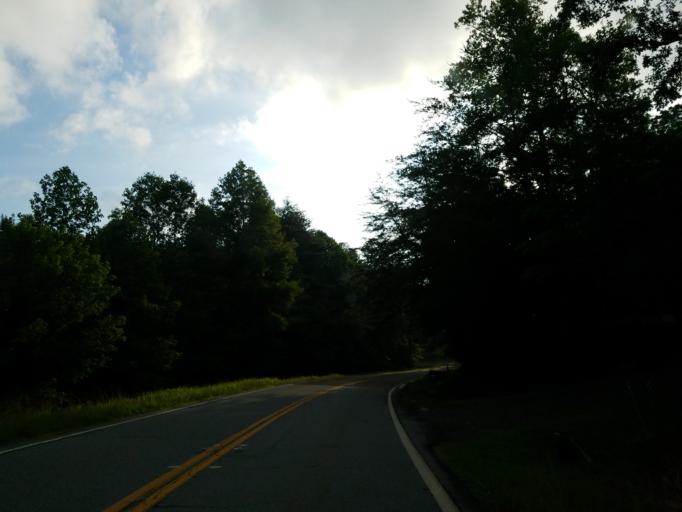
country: US
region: Georgia
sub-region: Fannin County
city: Blue Ridge
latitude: 34.7715
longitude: -84.1805
